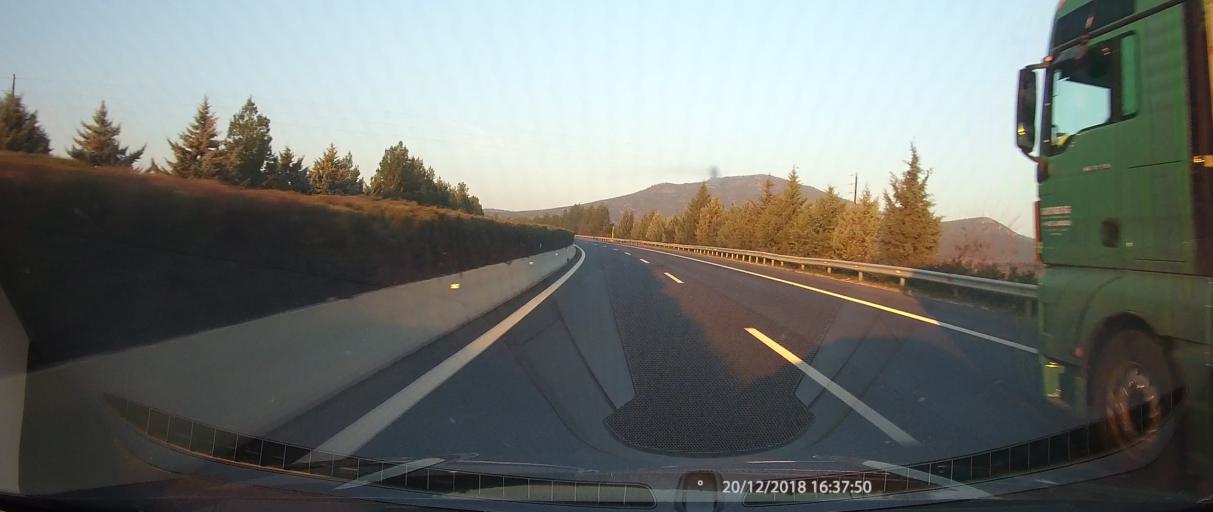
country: GR
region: Thessaly
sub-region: Nomos Magnisias
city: Velestino
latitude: 39.3351
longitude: 22.7816
